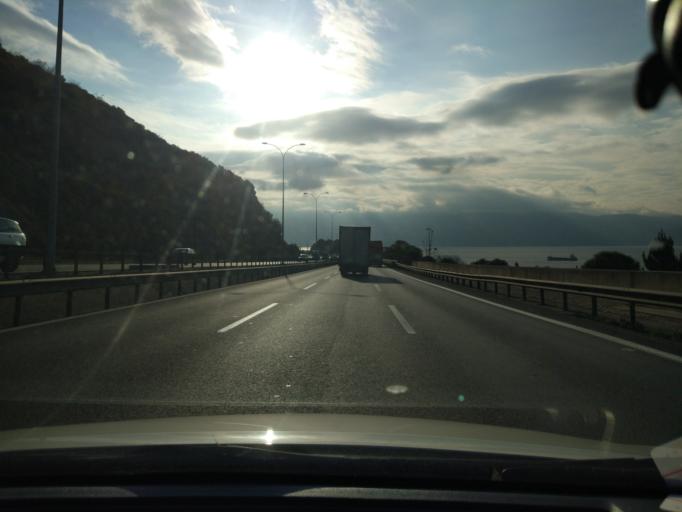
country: TR
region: Kocaeli
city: Hereke
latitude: 40.7813
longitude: 29.6283
